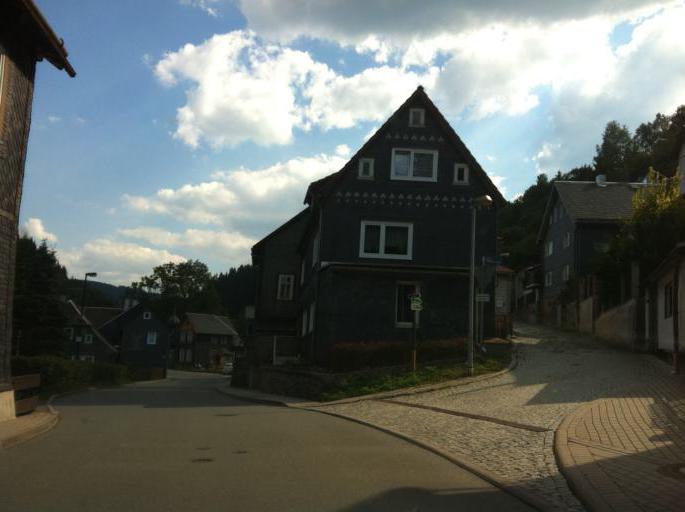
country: DE
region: Thuringia
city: Katzhutte
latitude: 50.5493
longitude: 11.0570
